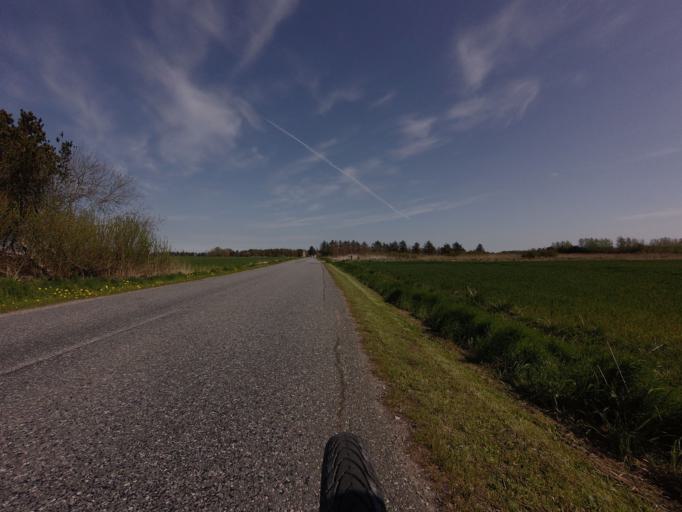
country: DK
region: North Denmark
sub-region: Jammerbugt Kommune
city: Pandrup
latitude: 57.2260
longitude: 9.6405
